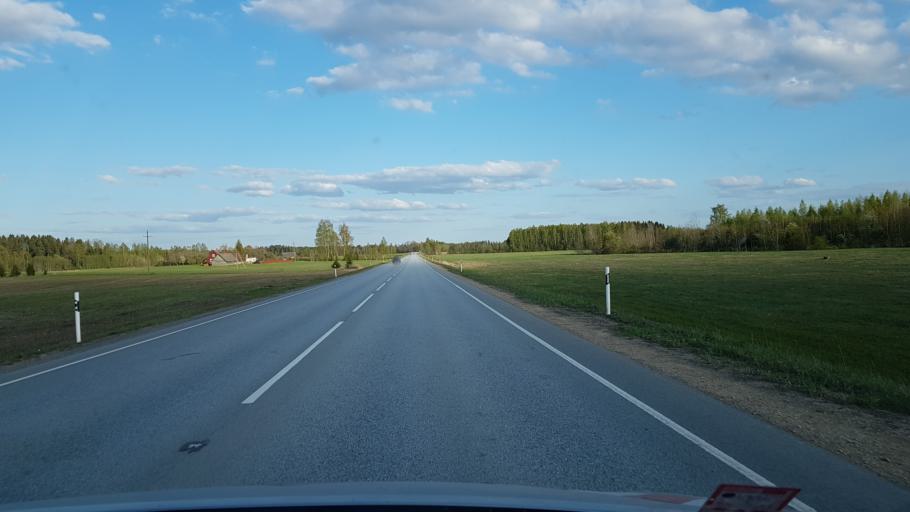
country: EE
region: Vorumaa
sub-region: Voru linn
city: Voru
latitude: 57.9130
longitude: 26.8205
